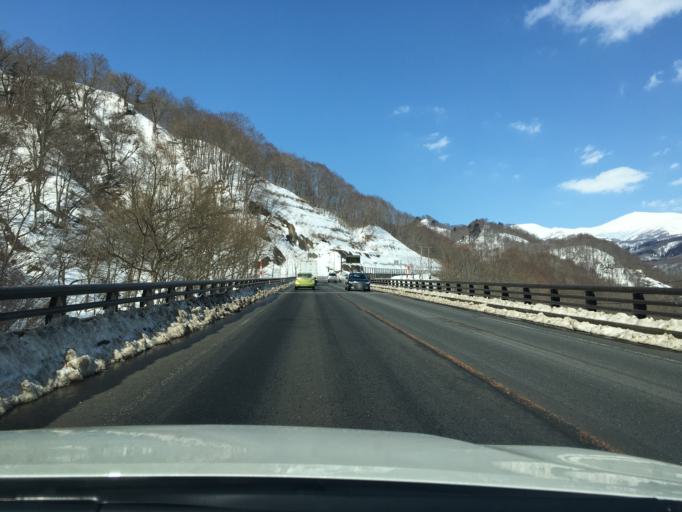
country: JP
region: Yamagata
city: Sagae
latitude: 38.4578
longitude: 139.9907
